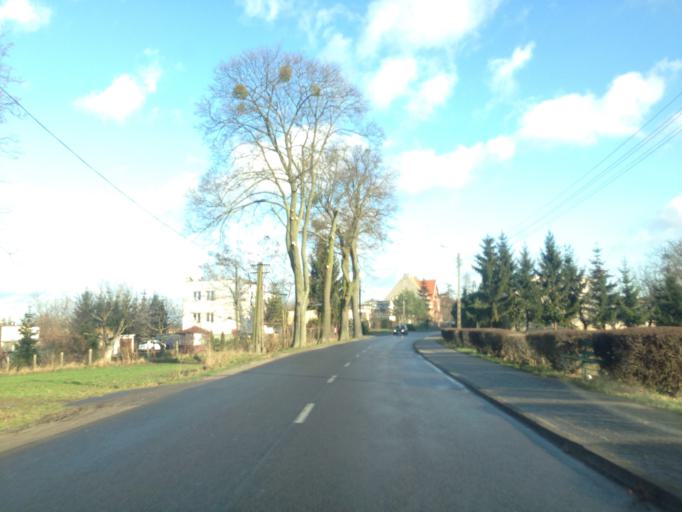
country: PL
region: Kujawsko-Pomorskie
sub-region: Powiat grudziadzki
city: Lasin
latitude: 53.5161
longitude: 19.0788
